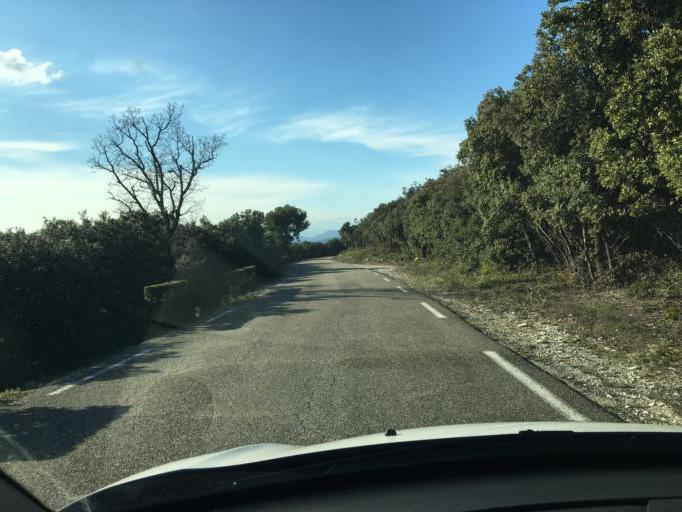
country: FR
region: Provence-Alpes-Cote d'Azur
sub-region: Departement du Vaucluse
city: Villes-sur-Auzon
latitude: 44.0360
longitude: 5.2578
